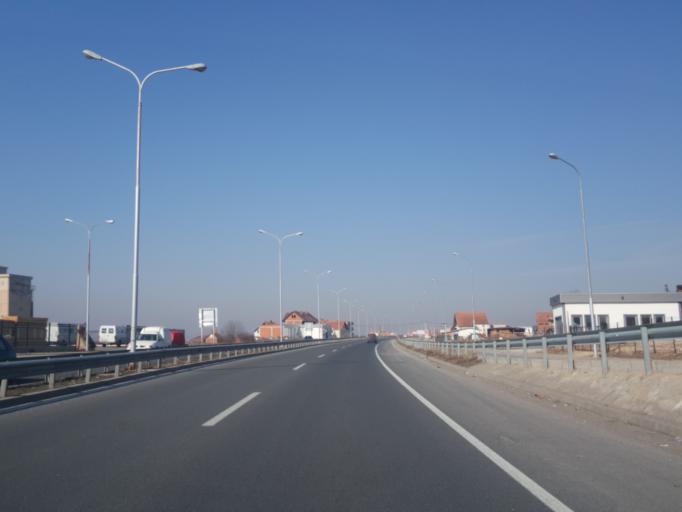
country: XK
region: Pristina
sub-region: Komuna e Obiliqit
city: Obiliq
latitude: 42.7395
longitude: 21.0537
